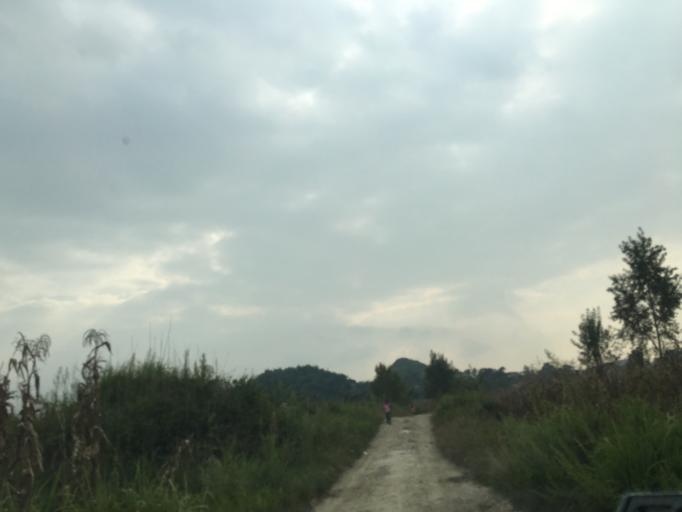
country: CN
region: Guangxi Zhuangzu Zizhiqu
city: Xinzhou
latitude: 25.4460
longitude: 105.6512
